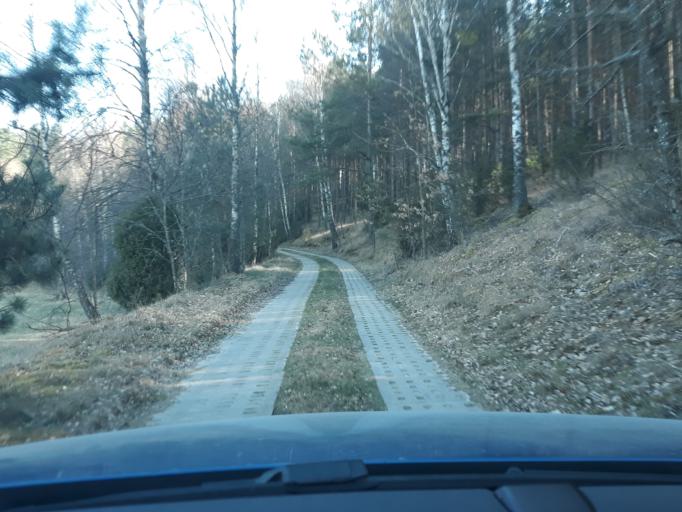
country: PL
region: Pomeranian Voivodeship
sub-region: Powiat bytowski
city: Lipnica
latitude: 53.9228
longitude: 17.4491
